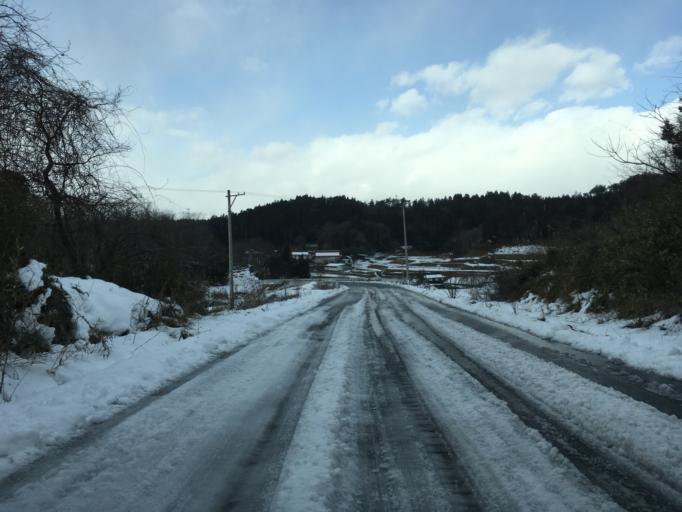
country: JP
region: Iwate
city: Ichinoseki
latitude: 38.8647
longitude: 141.1930
